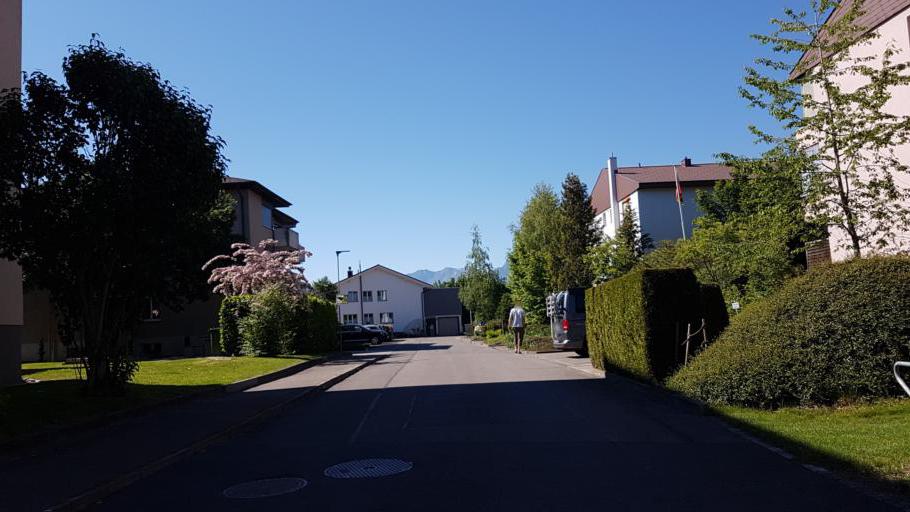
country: CH
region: Bern
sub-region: Bern-Mittelland District
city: Niederwichtrach
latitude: 46.8387
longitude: 7.5641
